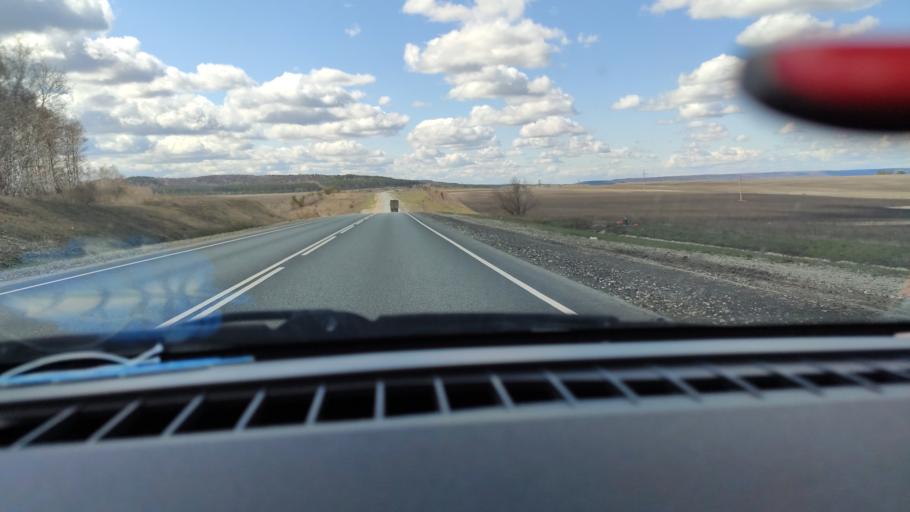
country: RU
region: Saratov
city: Khvalynsk
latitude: 52.5517
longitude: 48.0754
